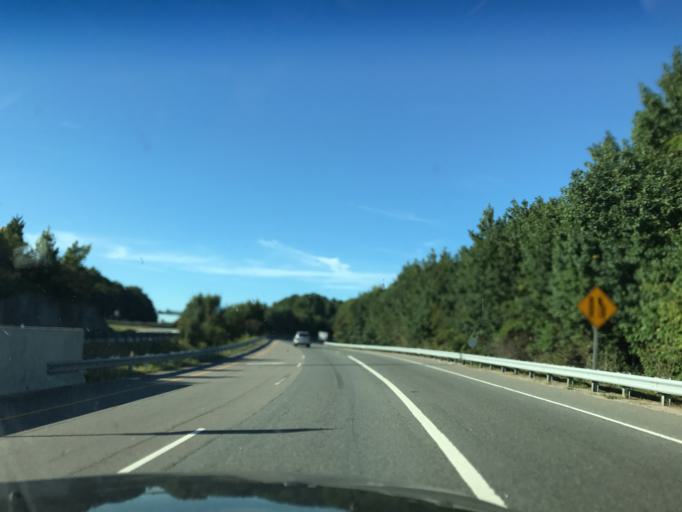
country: US
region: Virginia
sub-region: City of Chesapeake
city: Chesapeake
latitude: 36.7583
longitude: -76.2660
